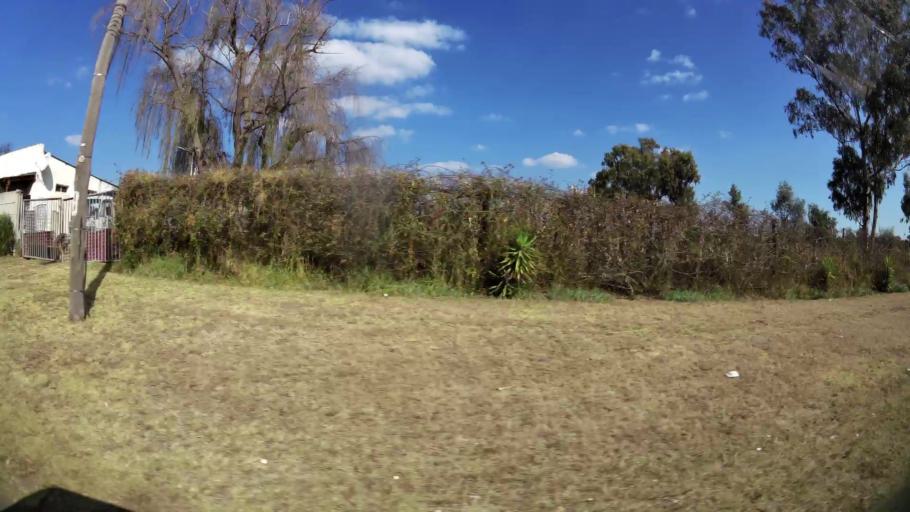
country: ZA
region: Gauteng
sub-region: Ekurhuleni Metropolitan Municipality
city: Benoni
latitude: -26.0976
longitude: 28.3501
